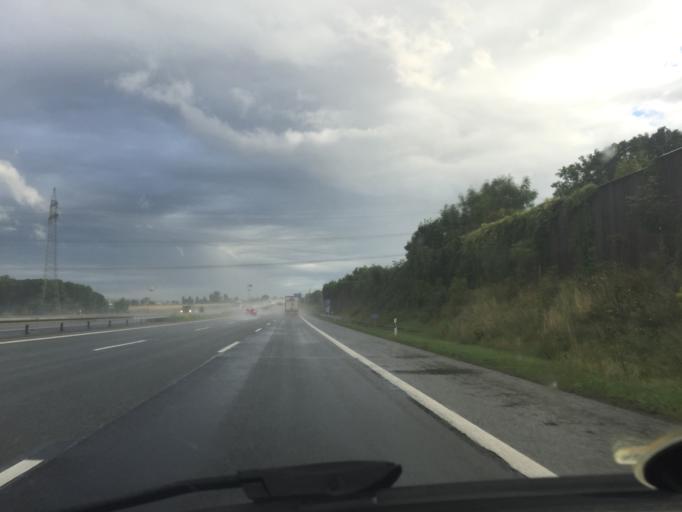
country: DE
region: Bavaria
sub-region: Upper Franconia
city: Munchberg
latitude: 50.2136
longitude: 11.7808
